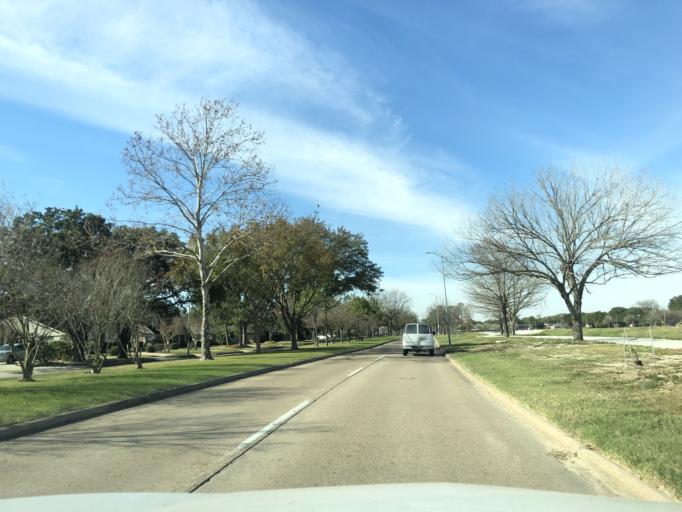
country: US
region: Texas
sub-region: Harris County
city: Bellaire
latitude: 29.6754
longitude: -95.4889
